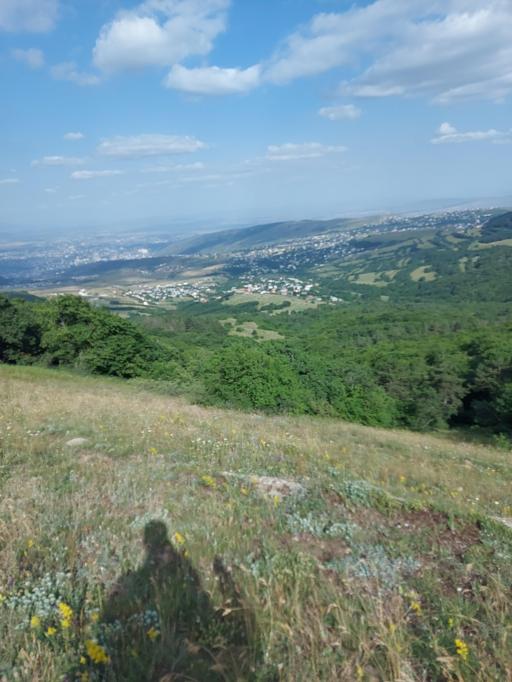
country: GE
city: Tsqnet'i
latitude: 41.6780
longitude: 44.7045
